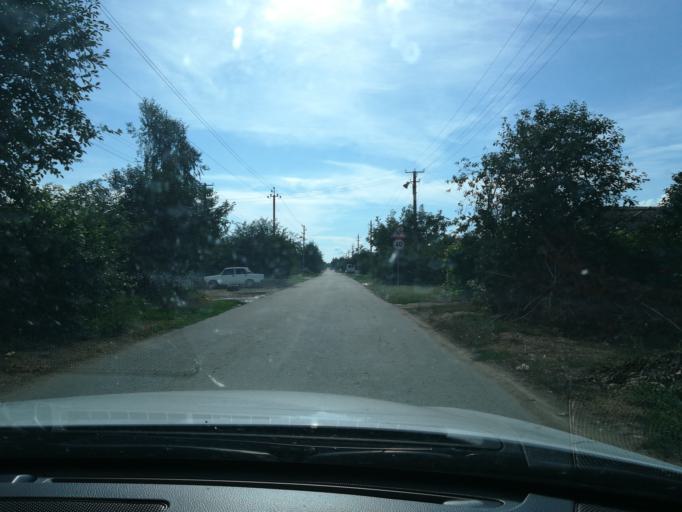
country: RU
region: Krasnodarskiy
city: Strelka
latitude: 45.1729
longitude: 37.2729
